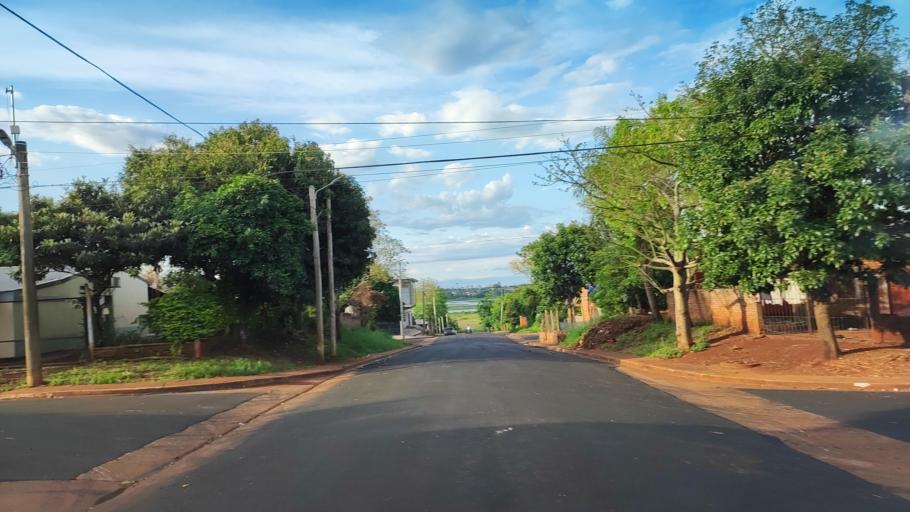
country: AR
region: Misiones
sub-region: Departamento de Capital
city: Posadas
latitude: -27.4347
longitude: -55.9071
